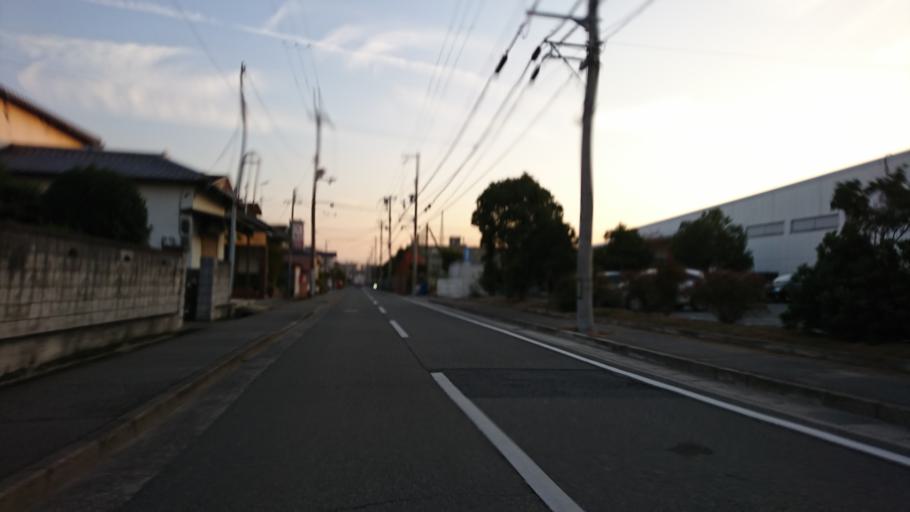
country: JP
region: Hyogo
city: Kakogawacho-honmachi
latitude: 34.7625
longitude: 134.8627
